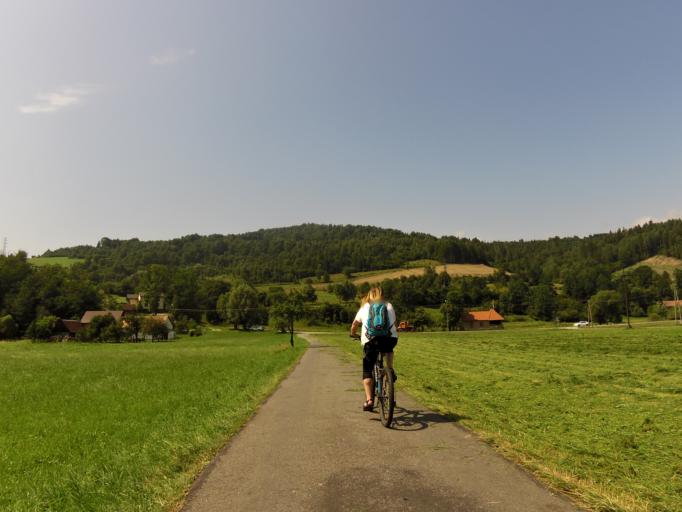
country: PL
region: Silesian Voivodeship
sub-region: Powiat zywiecki
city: Milowka
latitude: 49.5738
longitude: 19.0905
